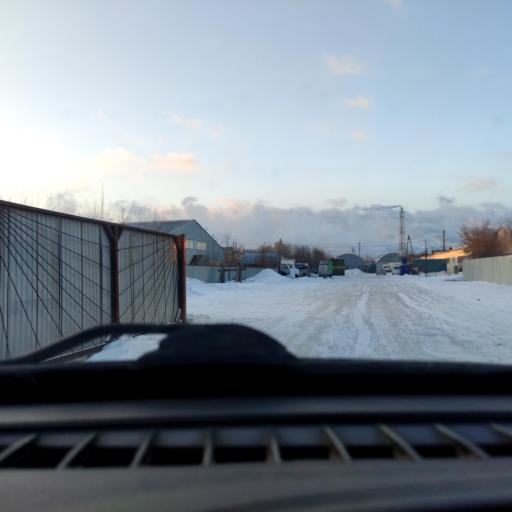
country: RU
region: Samara
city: Tol'yatti
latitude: 53.5653
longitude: 49.4848
